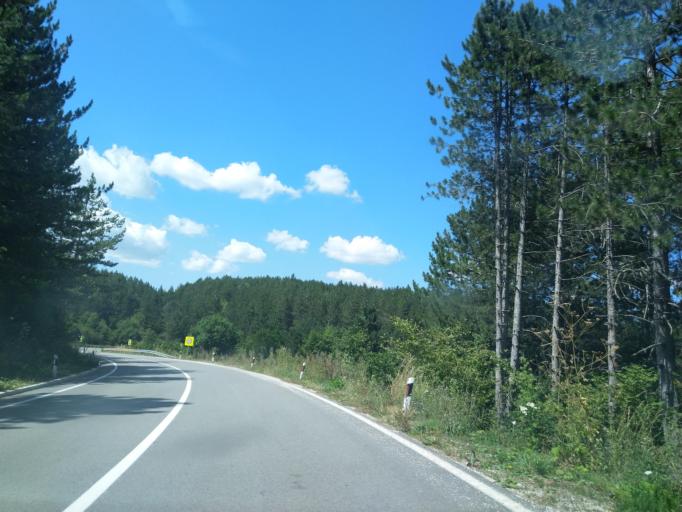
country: RS
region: Central Serbia
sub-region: Zlatiborski Okrug
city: Sjenica
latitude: 43.3070
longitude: 19.9002
